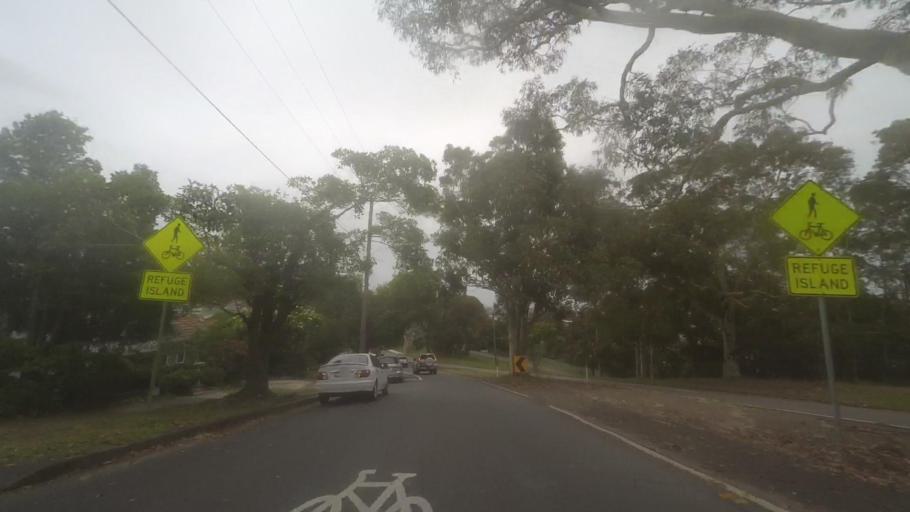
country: AU
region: New South Wales
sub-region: Lake Macquarie Shire
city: Highfields
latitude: -32.9456
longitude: 151.7151
